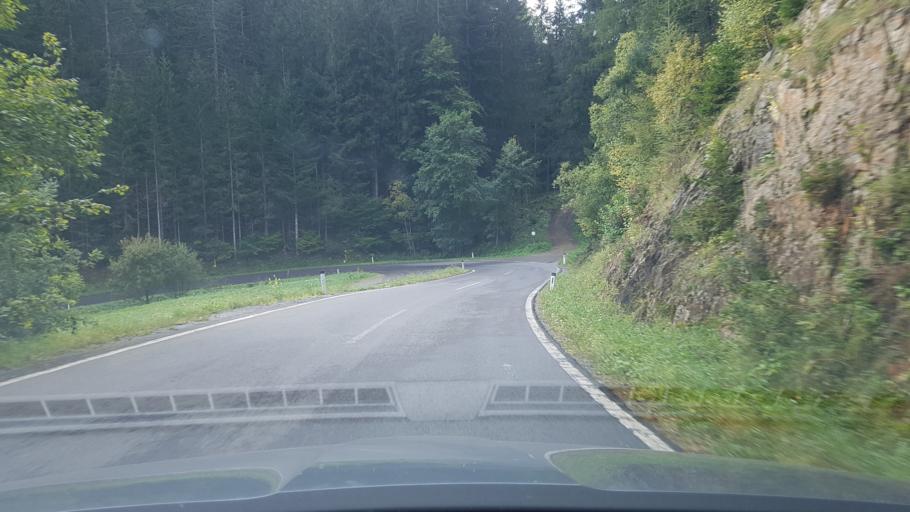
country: AT
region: Styria
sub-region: Politischer Bezirk Murau
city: Schoder
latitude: 47.1927
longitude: 14.1212
